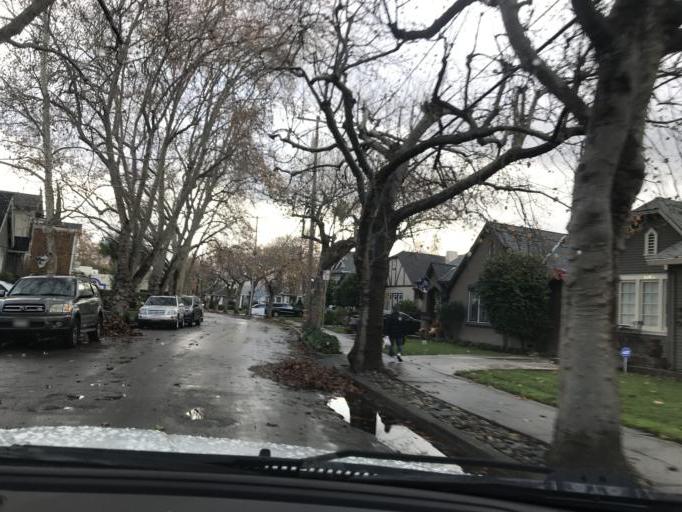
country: US
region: California
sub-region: Santa Clara County
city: Buena Vista
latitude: 37.3062
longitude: -121.9016
